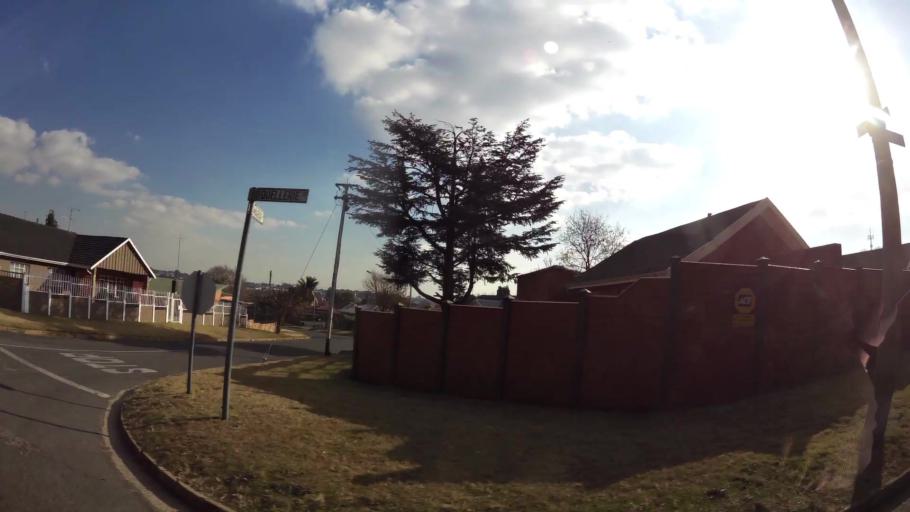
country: ZA
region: Gauteng
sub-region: West Rand District Municipality
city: Krugersdorp
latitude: -26.0913
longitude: 27.7602
